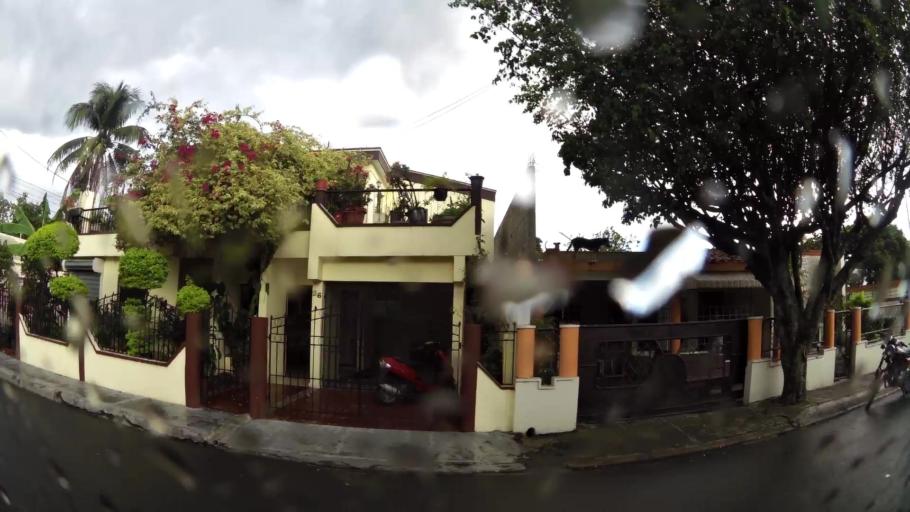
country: DO
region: Monsenor Nouel
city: Bonao
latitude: 18.9351
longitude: -70.4036
